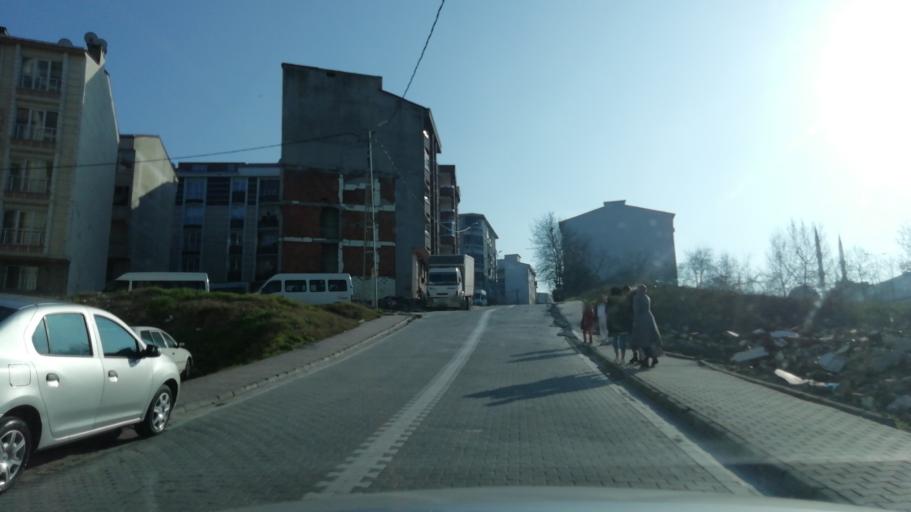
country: TR
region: Istanbul
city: Esenyurt
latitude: 41.0396
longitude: 28.6901
